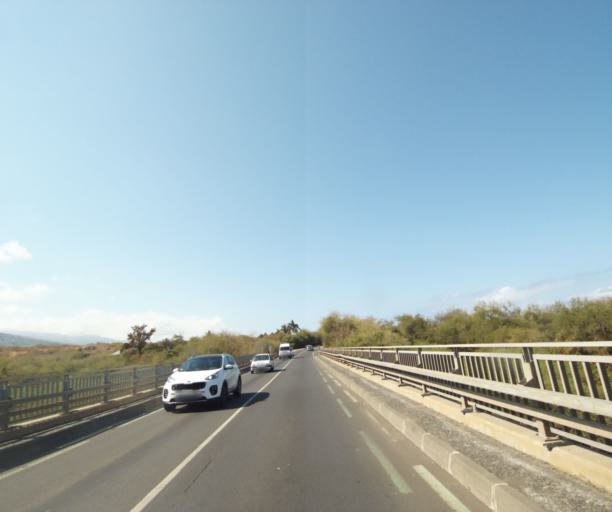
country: RE
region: Reunion
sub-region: Reunion
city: Trois-Bassins
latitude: -21.1095
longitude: 55.2558
